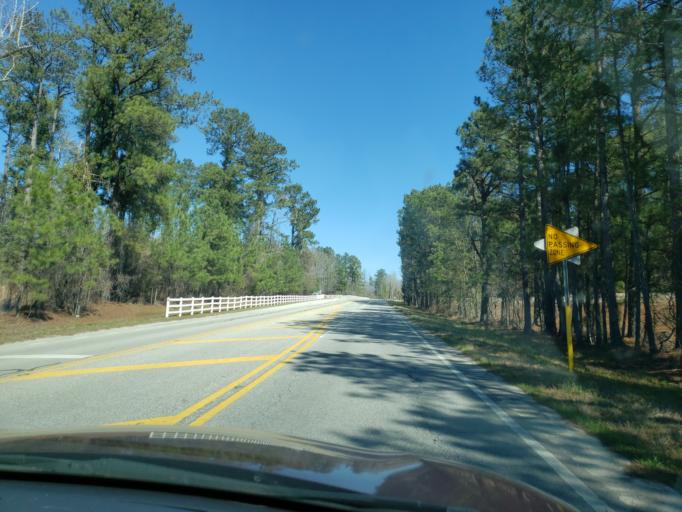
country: US
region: Alabama
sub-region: Lee County
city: Auburn
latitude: 32.5934
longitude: -85.6385
